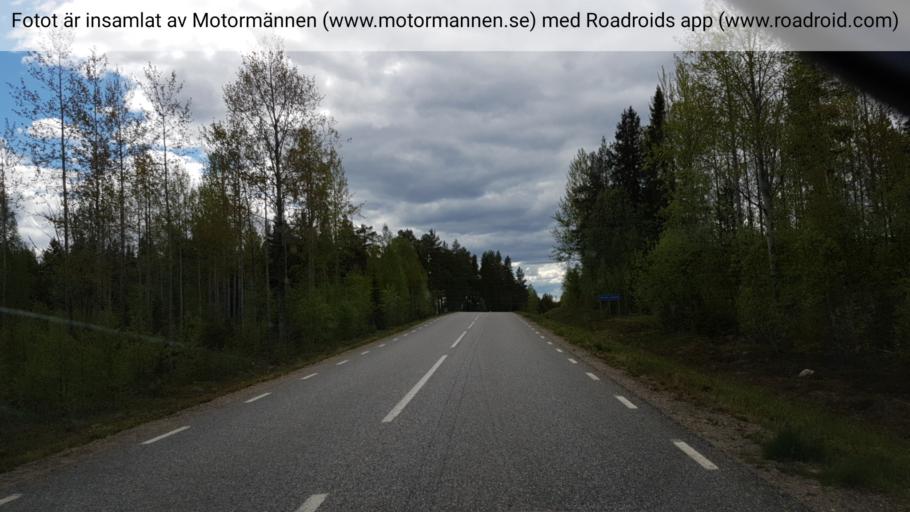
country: SE
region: Vaesterbotten
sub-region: Skelleftea Kommun
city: Langsele
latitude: 64.6256
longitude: 19.9813
